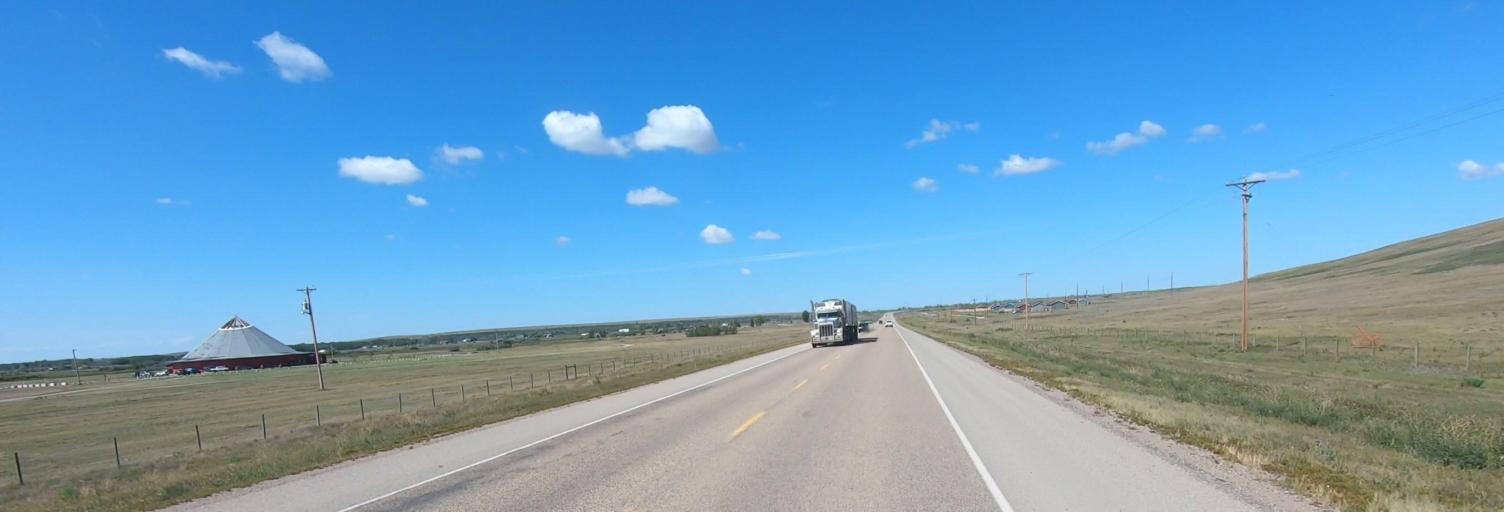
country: CA
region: Alberta
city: Strathmore
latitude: 50.8508
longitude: -113.1094
